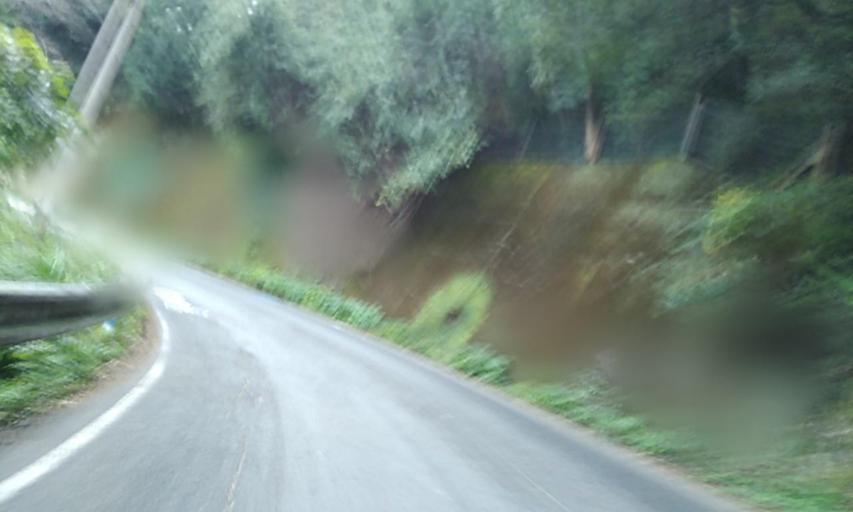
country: JP
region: Mie
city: Ise
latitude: 34.2909
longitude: 136.5336
